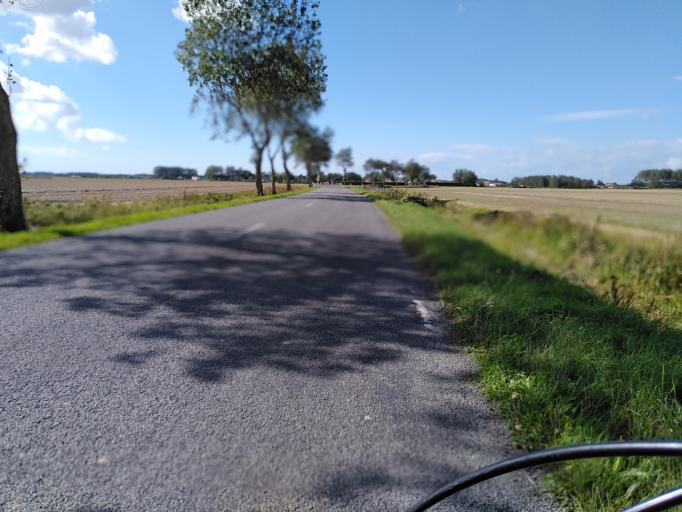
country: FR
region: Nord-Pas-de-Calais
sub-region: Departement du Nord
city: Grand-Fort-Philippe
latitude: 50.9896
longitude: 2.1047
